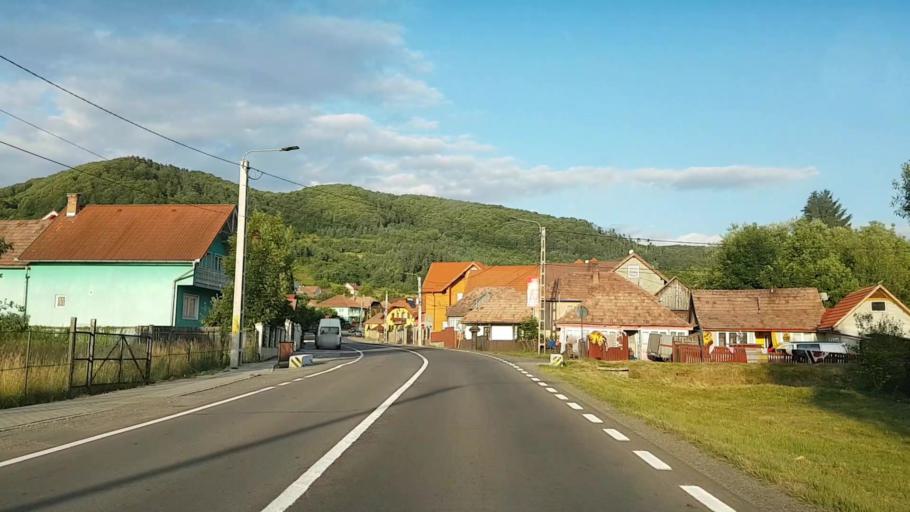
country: RO
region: Harghita
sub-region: Comuna Corund
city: Corund
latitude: 46.4697
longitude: 25.1947
